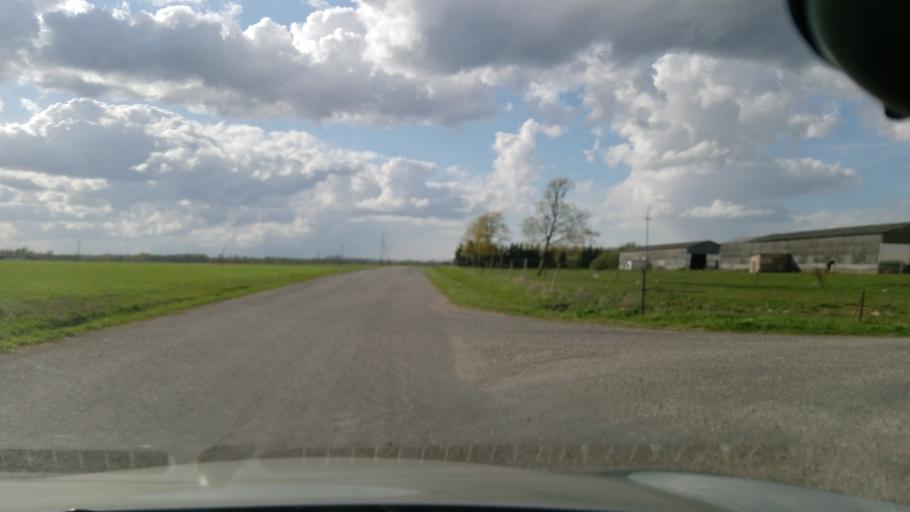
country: EE
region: Jaervamaa
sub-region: Jaerva-Jaani vald
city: Jarva-Jaani
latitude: 58.9490
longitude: 25.8238
